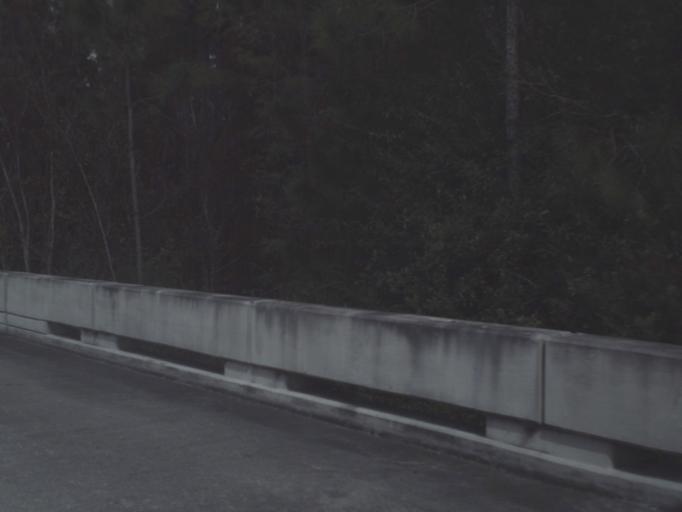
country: US
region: Florida
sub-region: Hillsborough County
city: Cheval
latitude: 28.1784
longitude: -82.5374
